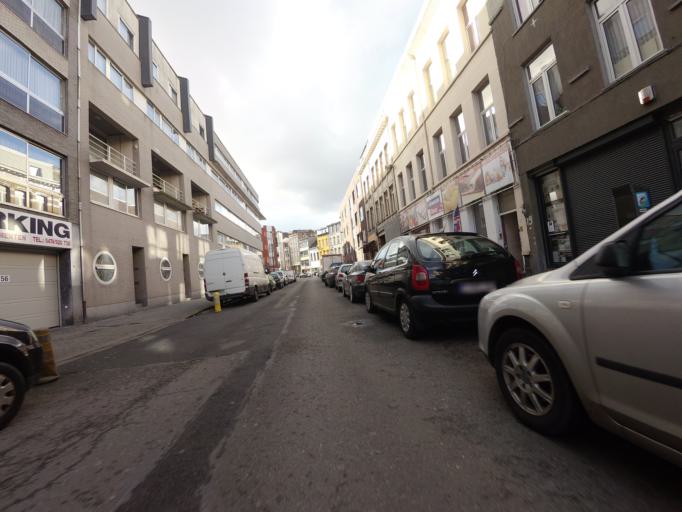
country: BE
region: Flanders
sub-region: Provincie Antwerpen
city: Antwerpen
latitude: 51.2227
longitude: 4.4228
